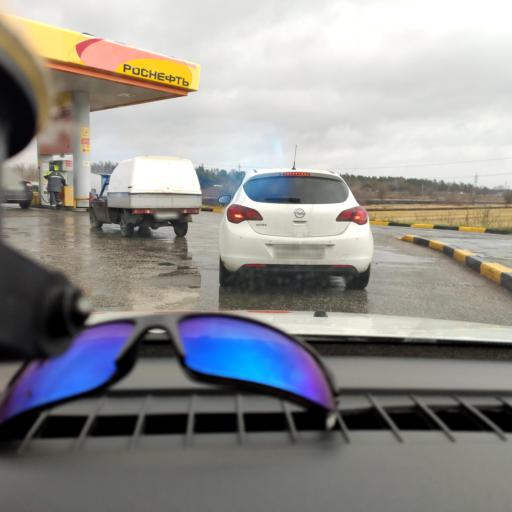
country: RU
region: Samara
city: Samara
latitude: 53.1240
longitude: 50.1701
